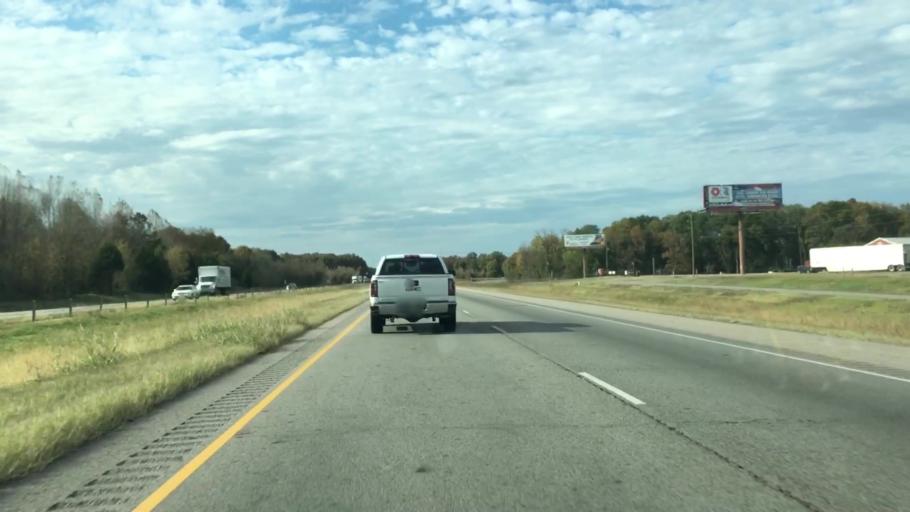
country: US
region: Arkansas
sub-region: Pope County
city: Atkins
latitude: 35.2243
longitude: -92.8365
